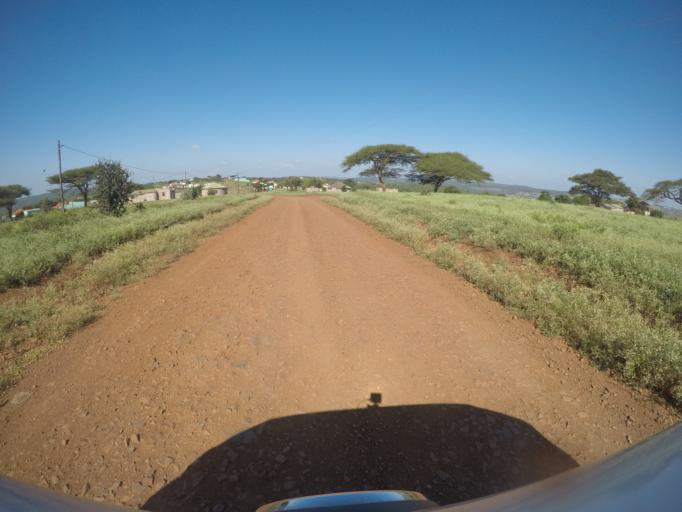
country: ZA
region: KwaZulu-Natal
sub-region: uThungulu District Municipality
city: Empangeni
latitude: -28.5724
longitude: 31.7278
